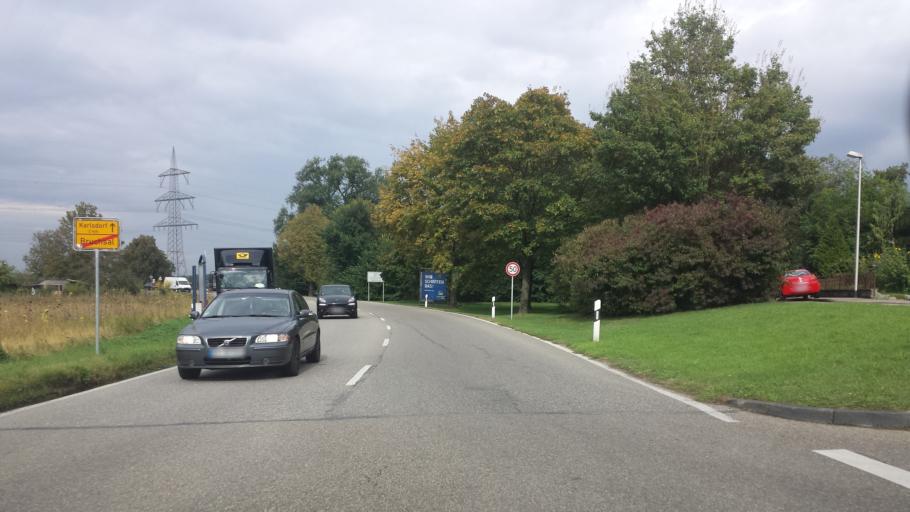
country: DE
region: Baden-Wuerttemberg
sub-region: Karlsruhe Region
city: Bruchsal
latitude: 49.1325
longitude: 8.5811
